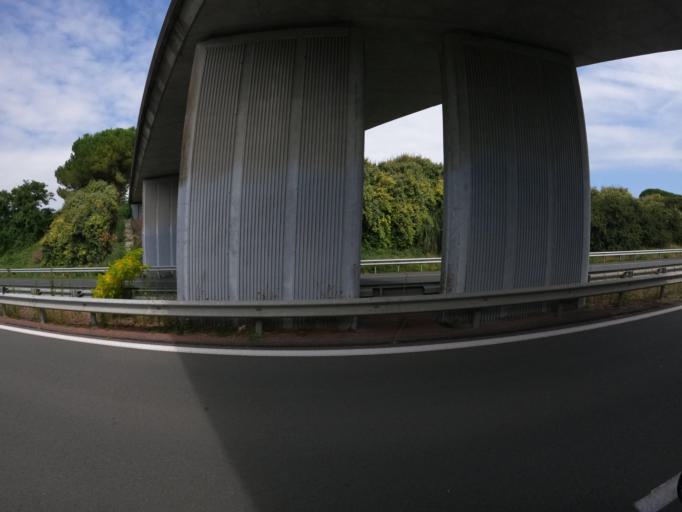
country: FR
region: Poitou-Charentes
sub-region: Departement de la Charente-Maritime
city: Courcon
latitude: 46.2237
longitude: -0.8484
